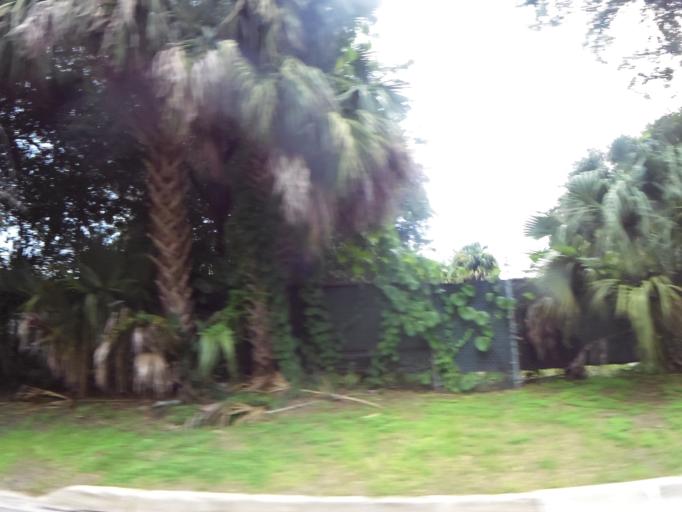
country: US
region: Florida
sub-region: Duval County
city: Jacksonville
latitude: 30.3496
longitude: -81.6445
